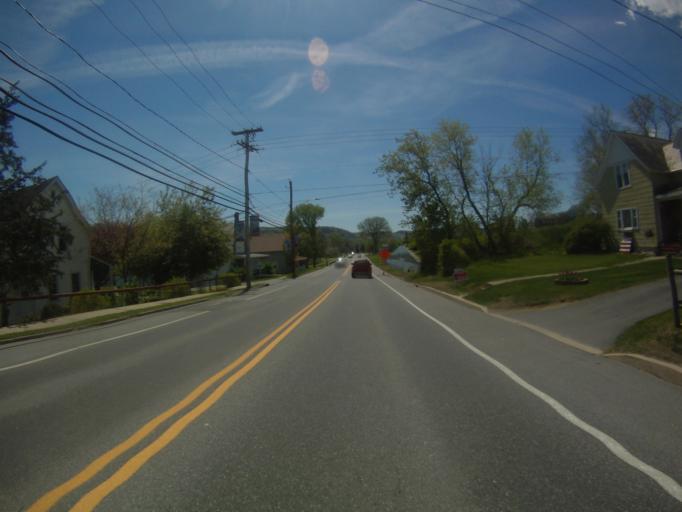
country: US
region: New York
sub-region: Essex County
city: Ticonderoga
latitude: 43.8508
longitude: -73.4363
